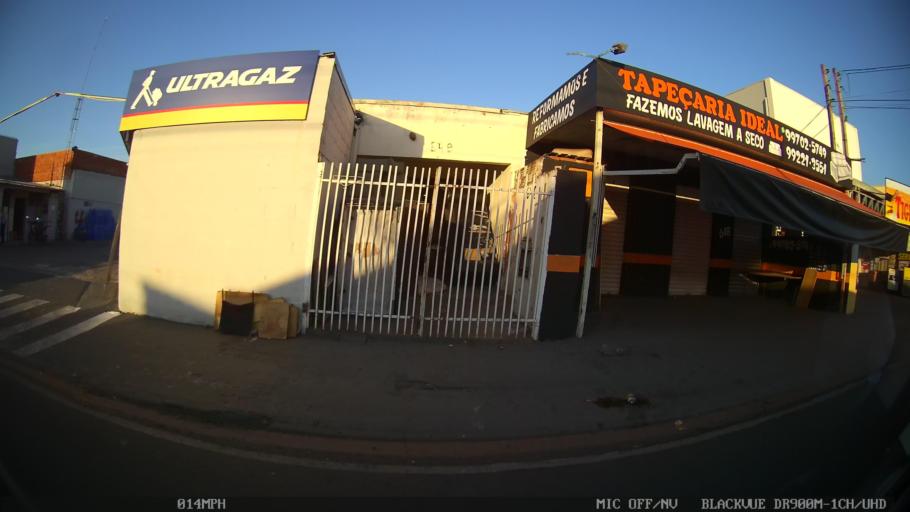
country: BR
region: Sao Paulo
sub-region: Sao Jose Do Rio Preto
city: Sao Jose do Rio Preto
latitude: -20.7923
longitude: -49.3696
